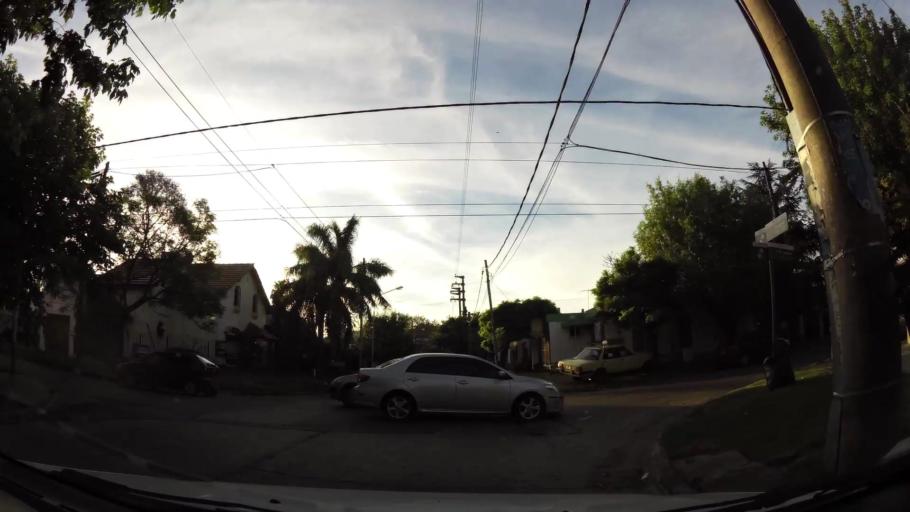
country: AR
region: Buenos Aires
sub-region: Partido de Moron
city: Moron
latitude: -34.6413
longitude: -58.6348
